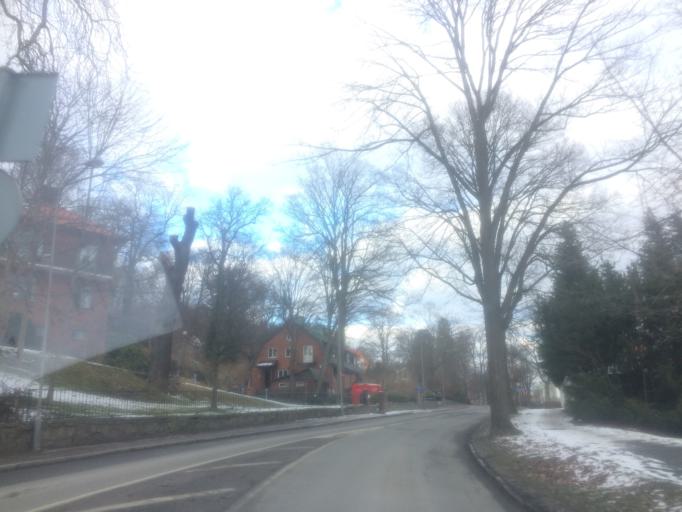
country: SE
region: Vaestra Goetaland
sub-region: Goteborg
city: Goeteborg
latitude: 57.6994
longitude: 11.9990
